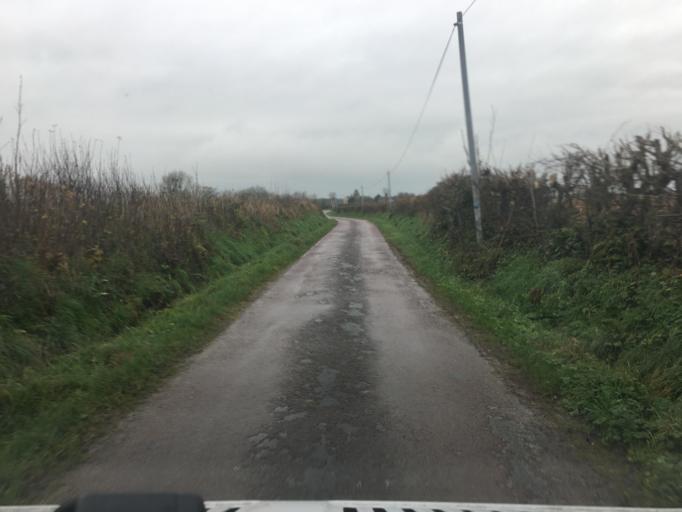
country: FR
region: Lower Normandy
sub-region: Departement de la Manche
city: Sainte-Mere-Eglise
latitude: 49.4310
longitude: -1.2620
